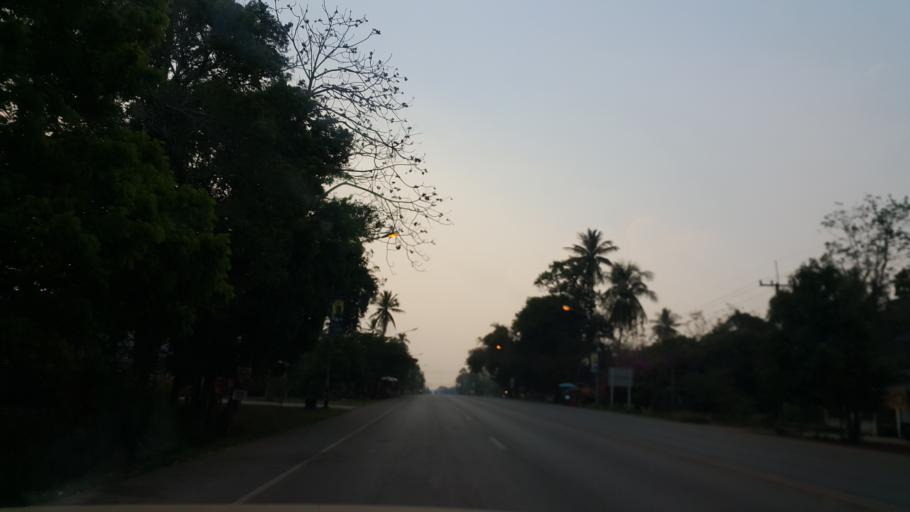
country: TH
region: Nakhon Phanom
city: Renu Nakhon
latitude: 17.0289
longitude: 104.7111
